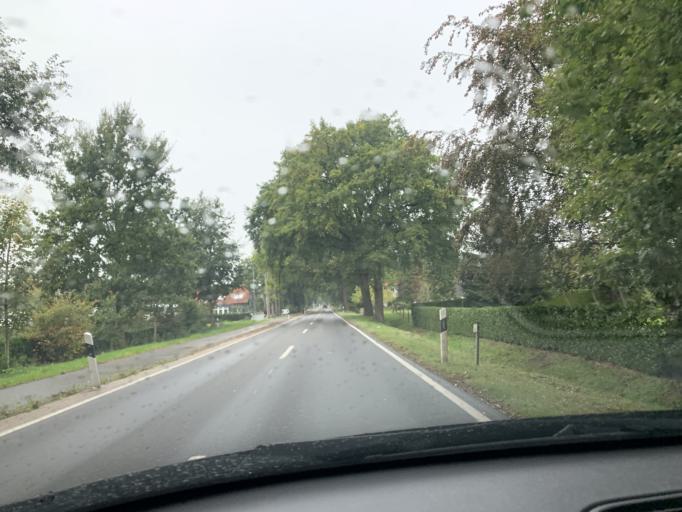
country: DE
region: Lower Saxony
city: Bad Zwischenahn
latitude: 53.1580
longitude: 8.0861
